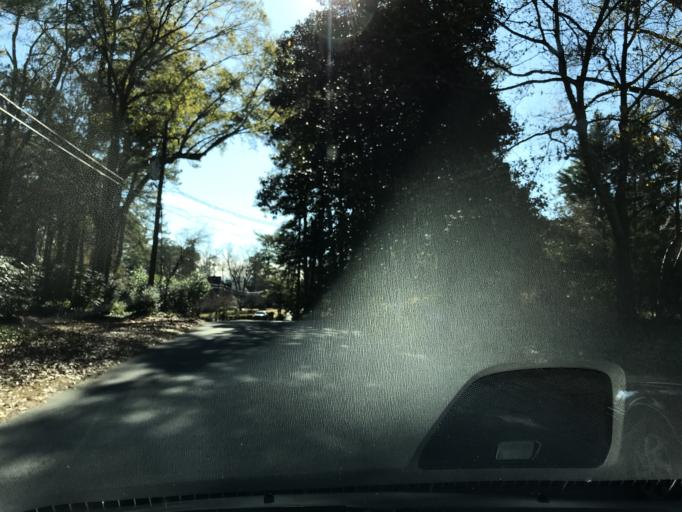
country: US
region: Georgia
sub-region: DeKalb County
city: North Atlanta
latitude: 33.8754
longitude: -84.3500
